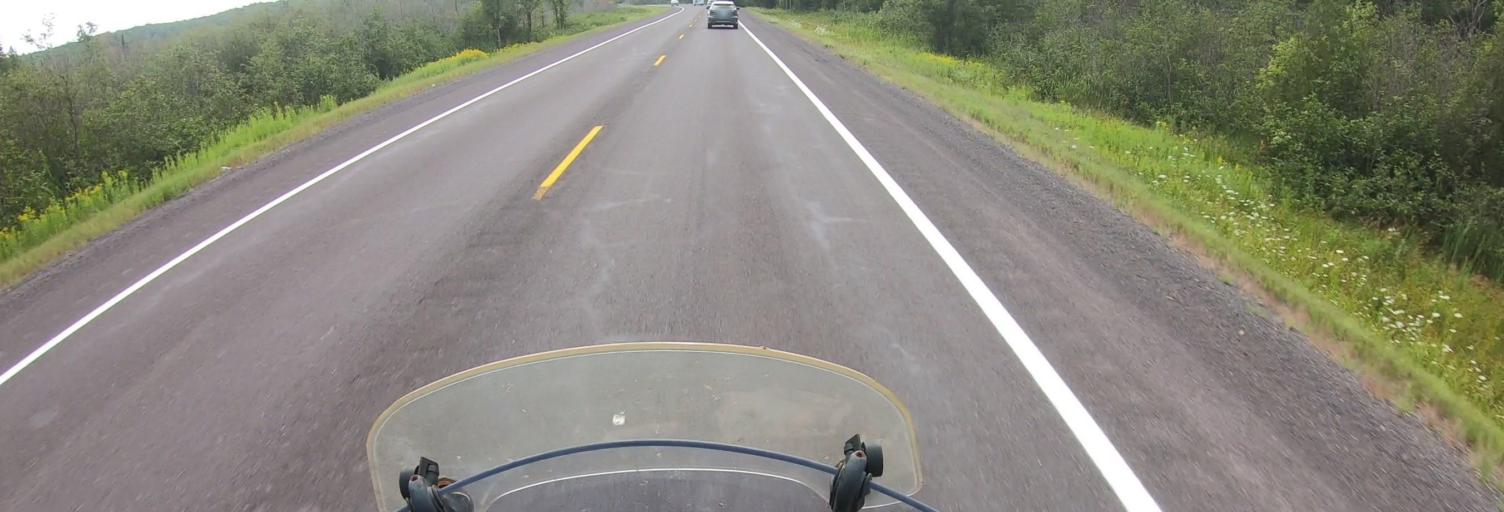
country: US
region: Michigan
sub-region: Houghton County
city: Hancock
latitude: 46.9277
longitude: -88.8065
